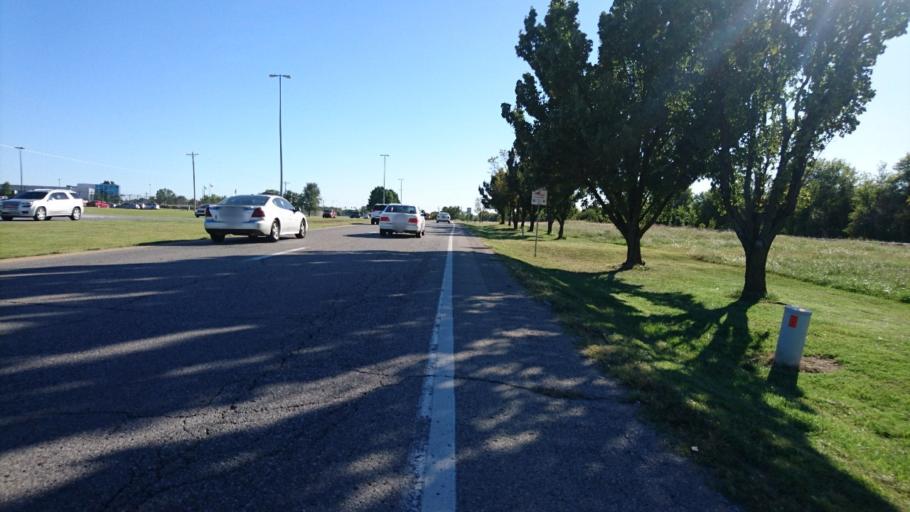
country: US
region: Oklahoma
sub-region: Rogers County
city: Claremore
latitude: 36.3329
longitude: -95.6047
